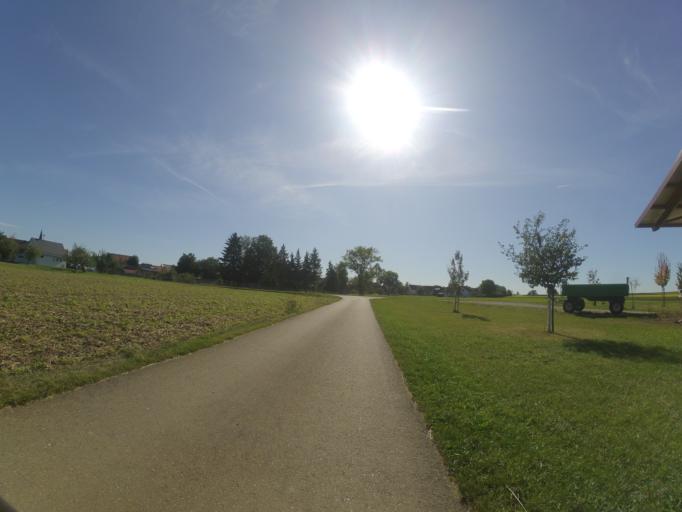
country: DE
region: Baden-Wuerttemberg
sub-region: Tuebingen Region
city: Nerenstetten
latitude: 48.5301
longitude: 10.0960
